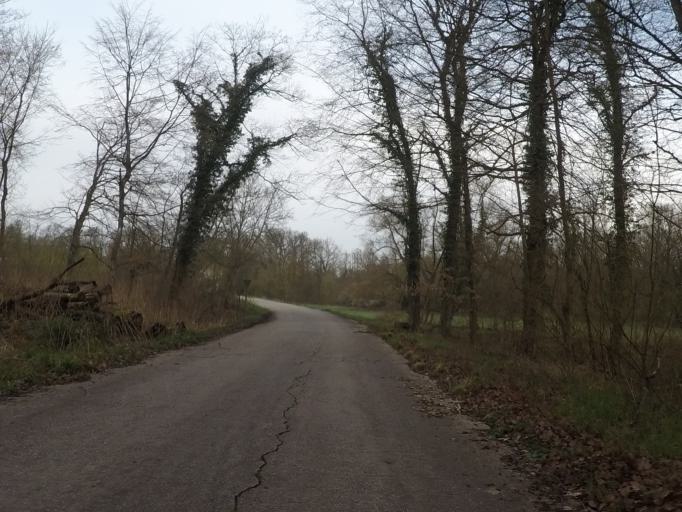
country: DE
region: Rheinland-Pfalz
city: Kandel
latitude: 49.0749
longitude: 8.2114
